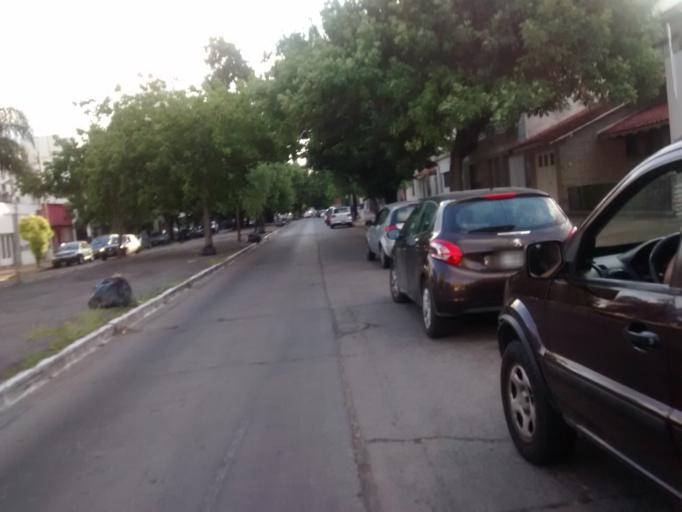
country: AR
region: Buenos Aires
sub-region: Partido de La Plata
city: La Plata
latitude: -34.9085
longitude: -57.9653
